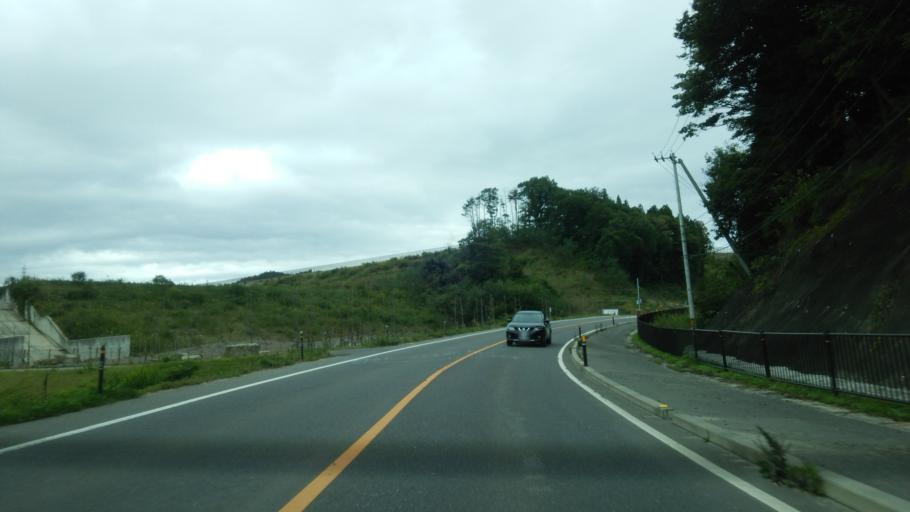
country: JP
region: Fukushima
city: Sukagawa
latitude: 37.1583
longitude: 140.2176
